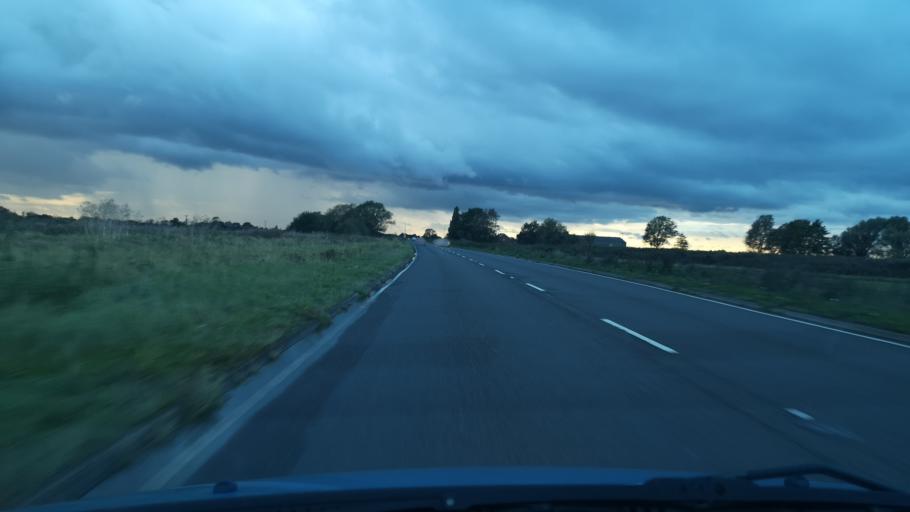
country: GB
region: England
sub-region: North Lincolnshire
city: Gunness
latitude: 53.5792
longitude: -0.7752
